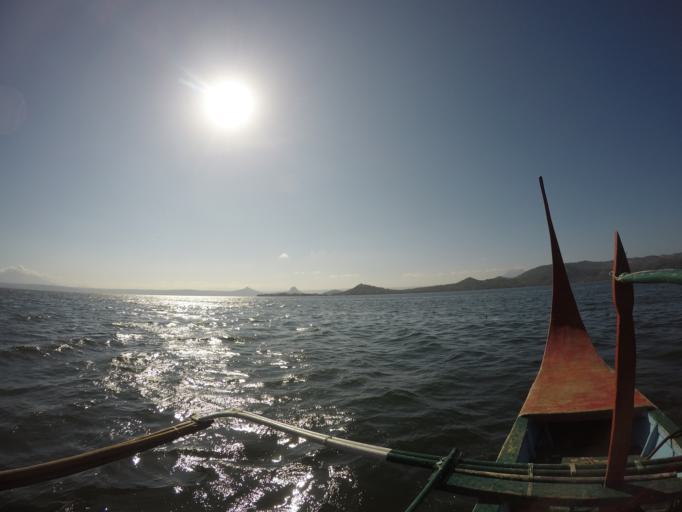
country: PH
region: Calabarzon
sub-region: Province of Batangas
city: Sampaloc
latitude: 14.0525
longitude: 120.9982
